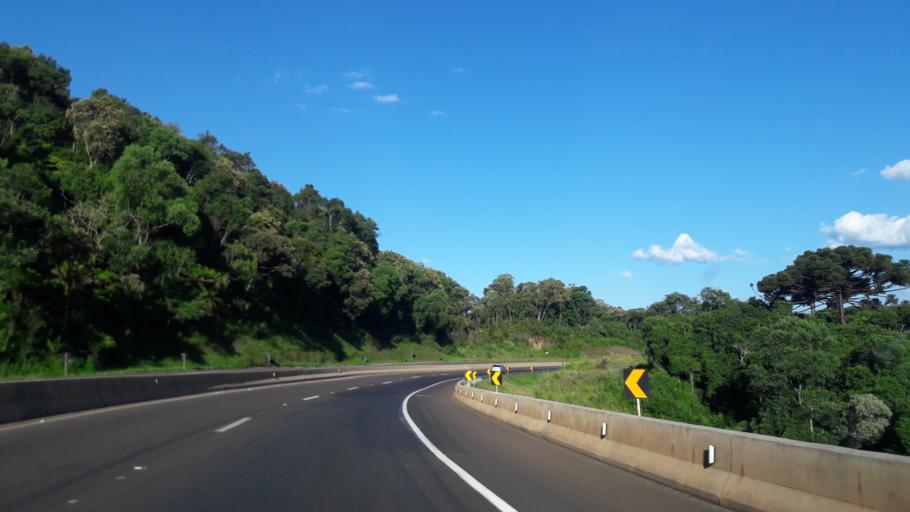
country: BR
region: Parana
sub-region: Guarapuava
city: Guarapuava
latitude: -25.3460
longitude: -51.3860
